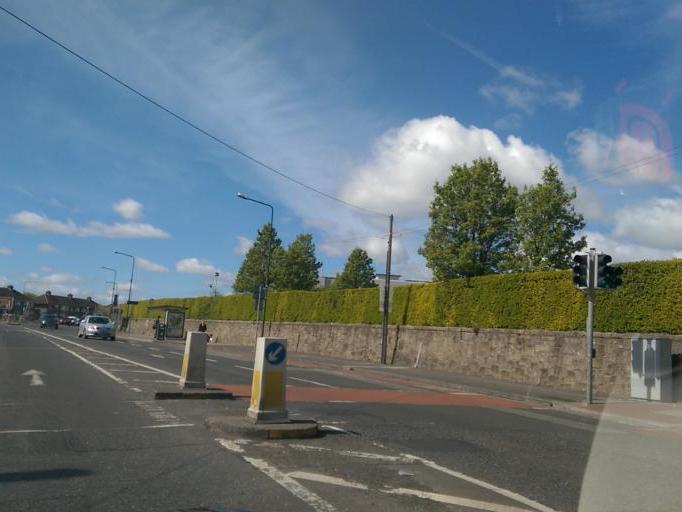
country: IE
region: Leinster
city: Crumlin
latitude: 53.3259
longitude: -6.3160
